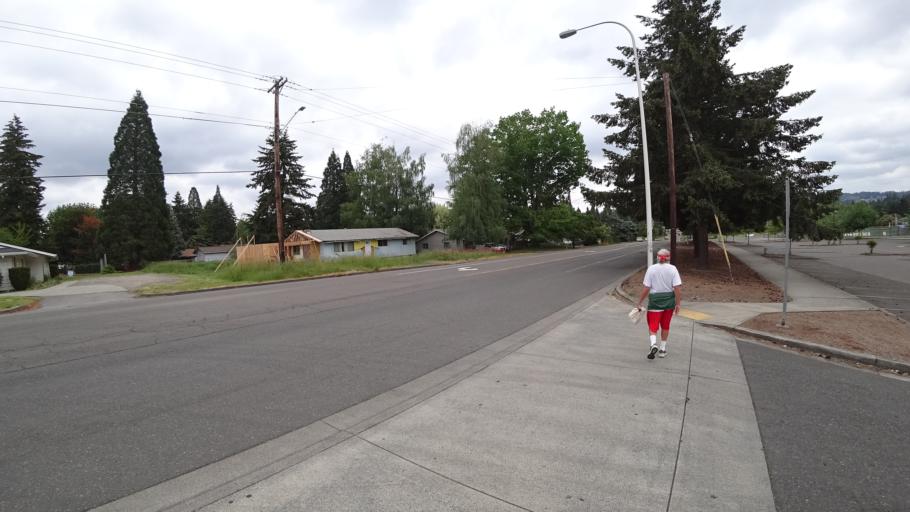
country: US
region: Oregon
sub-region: Washington County
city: Aloha
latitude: 45.4837
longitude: -122.8675
